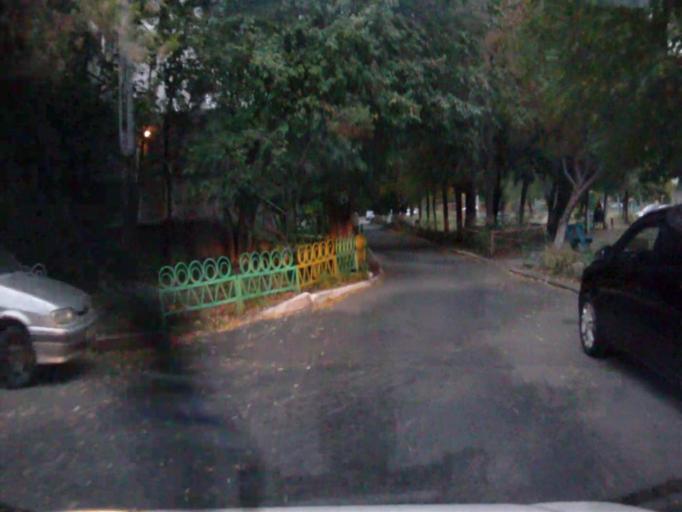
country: RU
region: Chelyabinsk
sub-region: Gorod Chelyabinsk
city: Chelyabinsk
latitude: 55.1898
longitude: 61.3364
